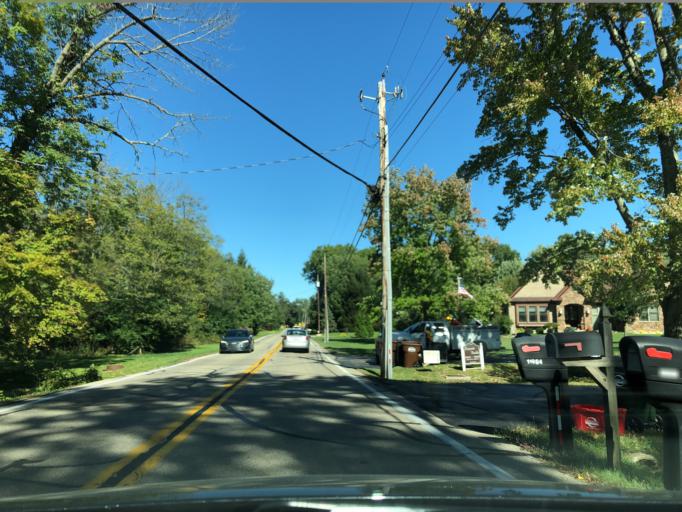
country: US
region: Ohio
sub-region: Hamilton County
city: Sixteen Mile Stand
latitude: 39.2783
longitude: -84.3113
